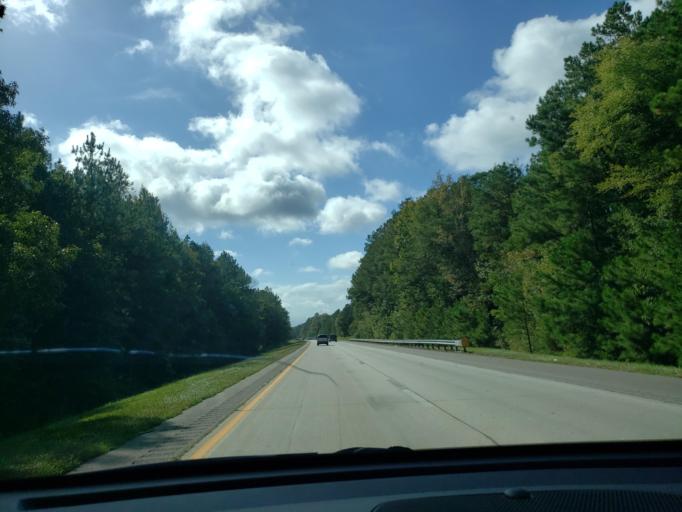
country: US
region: North Carolina
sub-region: Granville County
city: Oxford
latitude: 36.3217
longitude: -78.5212
